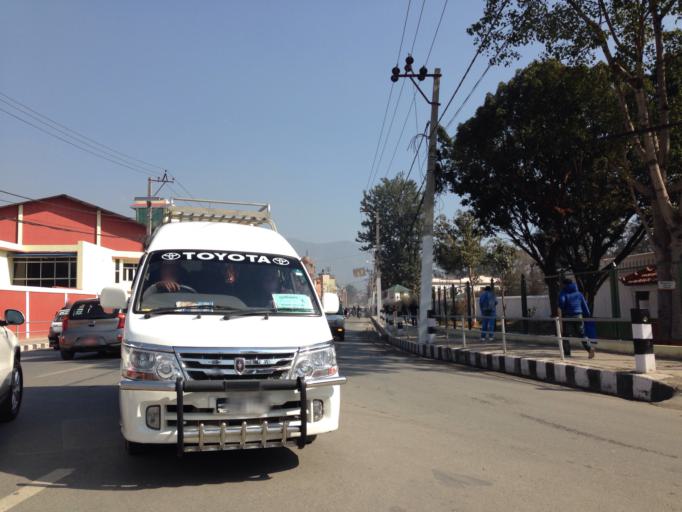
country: NP
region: Central Region
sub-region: Bagmati Zone
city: Kathmandu
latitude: 27.7329
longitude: 85.3289
